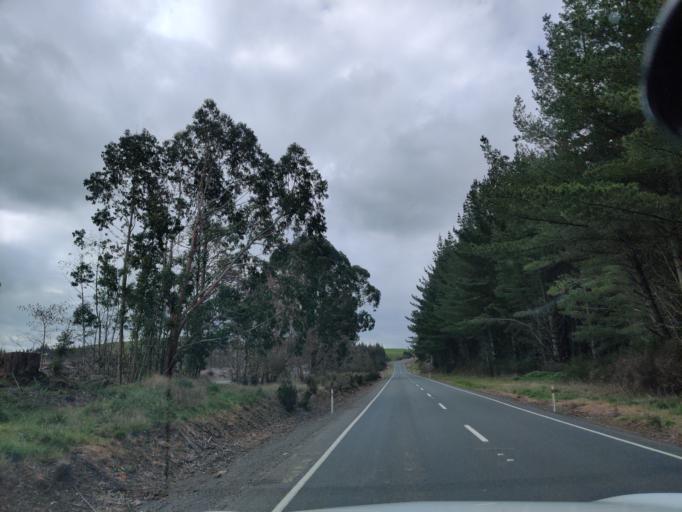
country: NZ
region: Waikato
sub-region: South Waikato District
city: Tokoroa
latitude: -38.2817
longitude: 175.8273
